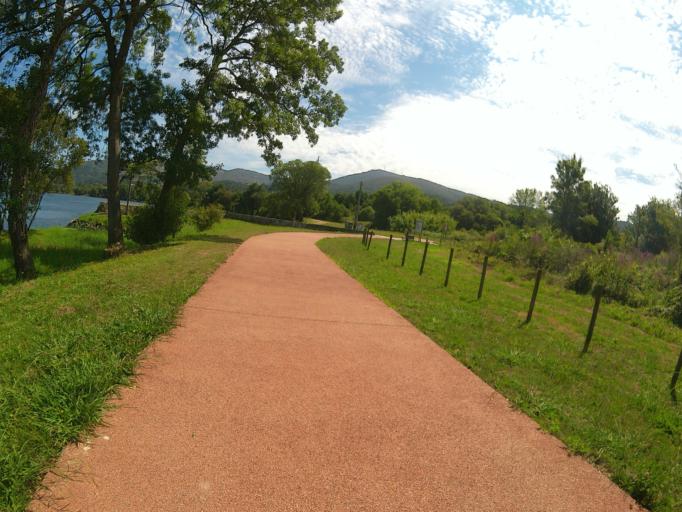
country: PT
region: Viana do Castelo
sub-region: Vila Nova de Cerveira
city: Vila Nova de Cerveira
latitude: 41.9245
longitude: -8.7604
